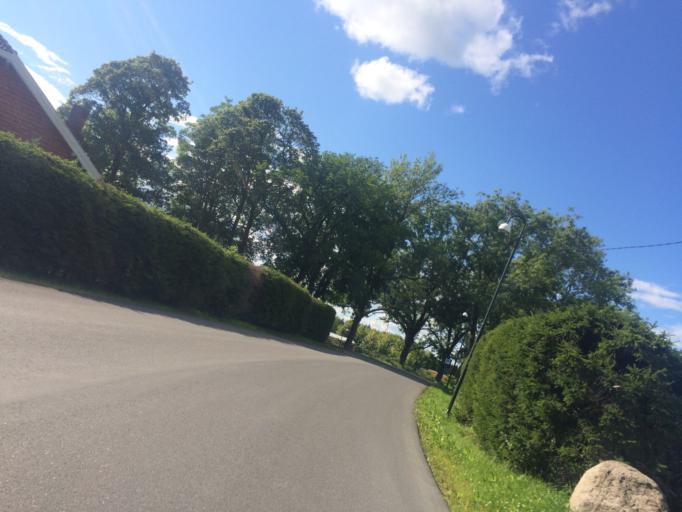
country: NO
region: Akershus
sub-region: As
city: As
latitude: 59.6689
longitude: 10.7715
